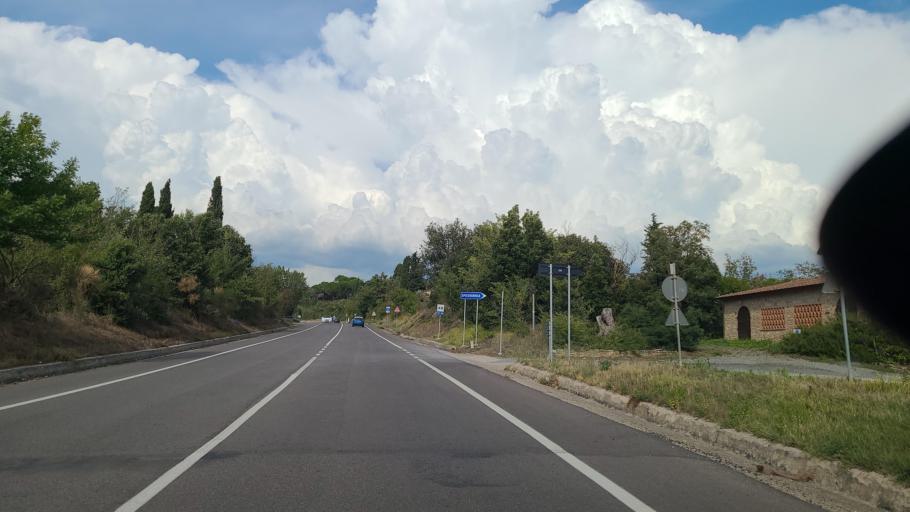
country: IT
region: Tuscany
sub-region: Province of Pisa
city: Volterra
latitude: 43.3898
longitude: 10.9513
